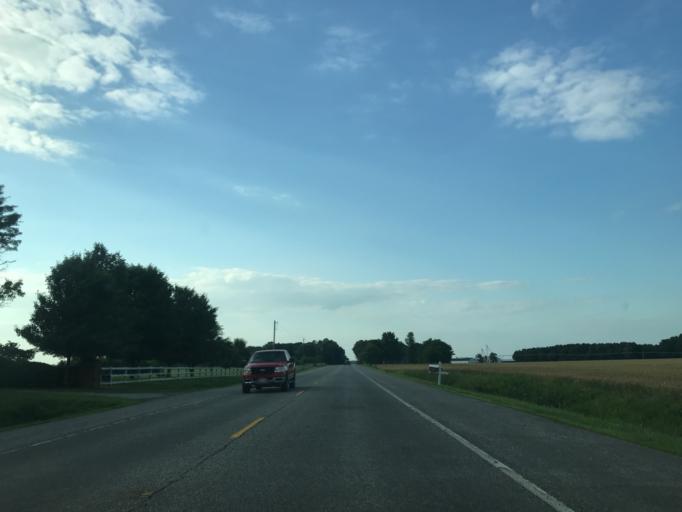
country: US
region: Maryland
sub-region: Caroline County
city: Denton
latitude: 38.7967
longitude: -75.7865
